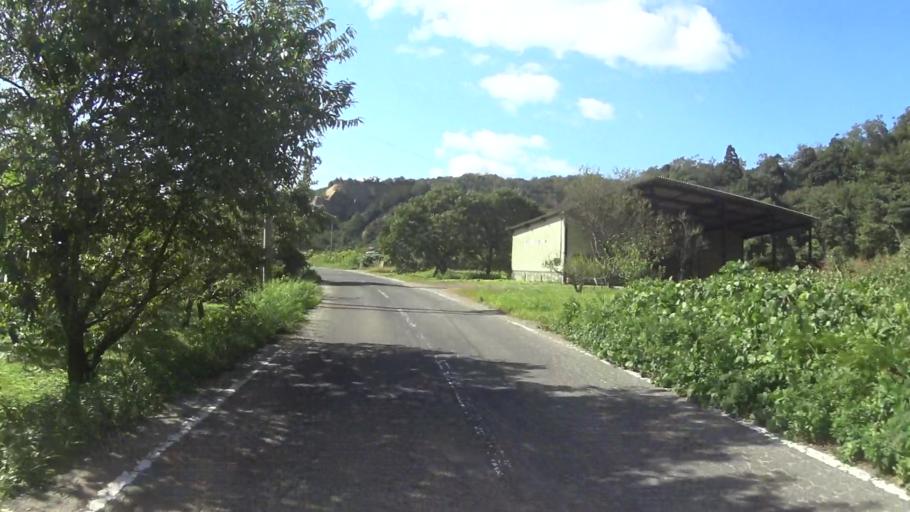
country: JP
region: Kyoto
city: Miyazu
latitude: 35.7011
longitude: 135.1023
